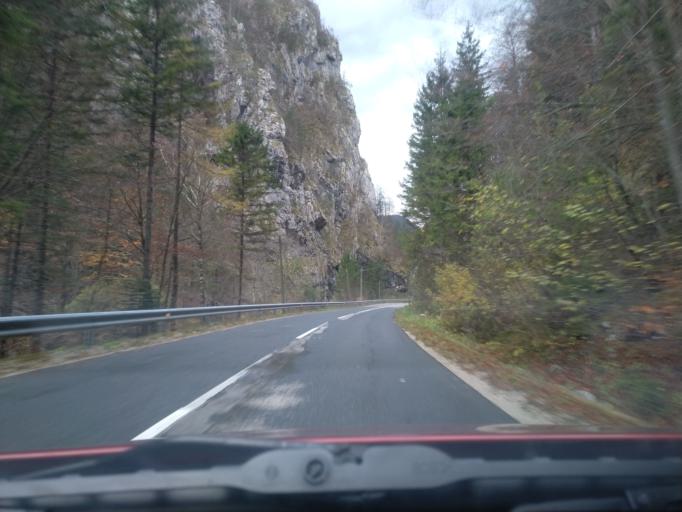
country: SI
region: Luce
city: Luce
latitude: 46.3819
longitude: 14.7268
